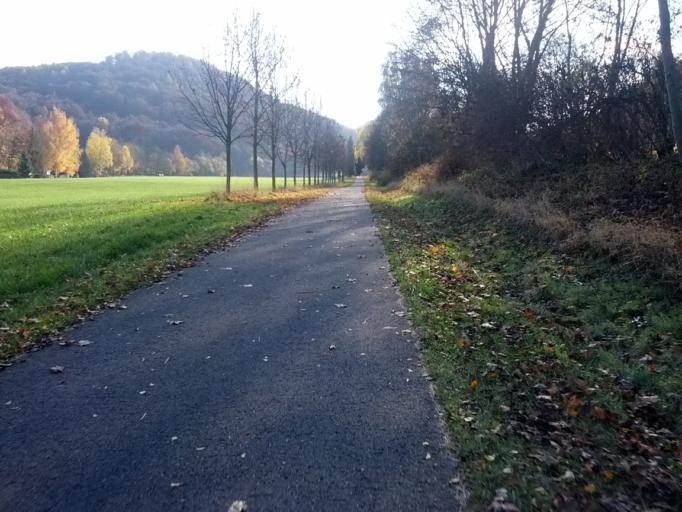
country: DE
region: Thuringia
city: Thal
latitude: 50.9302
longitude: 10.3936
